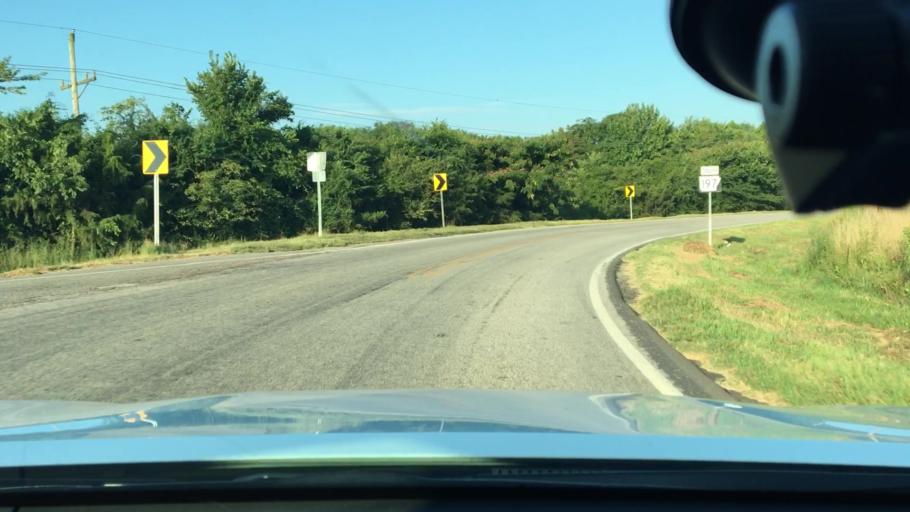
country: US
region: Arkansas
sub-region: Johnson County
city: Coal Hill
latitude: 35.3372
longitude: -93.6040
